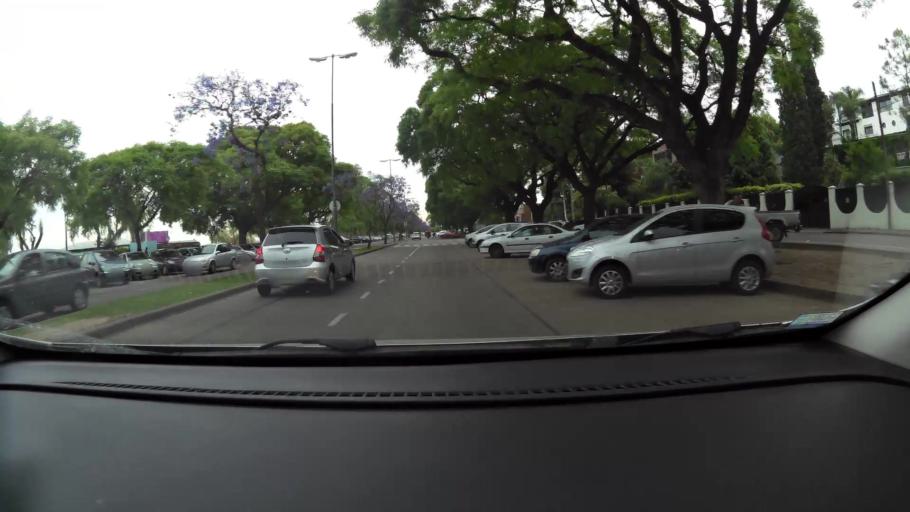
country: AR
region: Santa Fe
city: Granadero Baigorria
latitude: -32.8905
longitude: -60.6864
